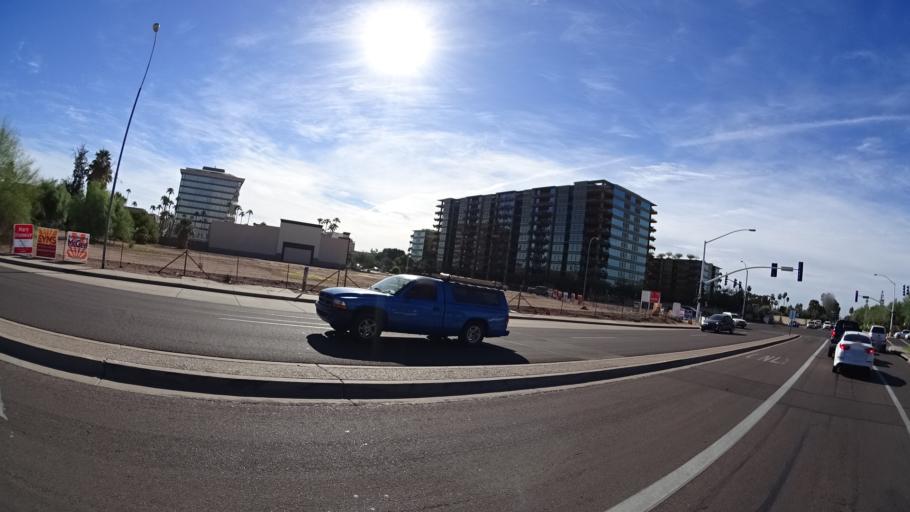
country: US
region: Arizona
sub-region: Maricopa County
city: Paradise Valley
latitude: 33.5028
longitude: -111.9347
